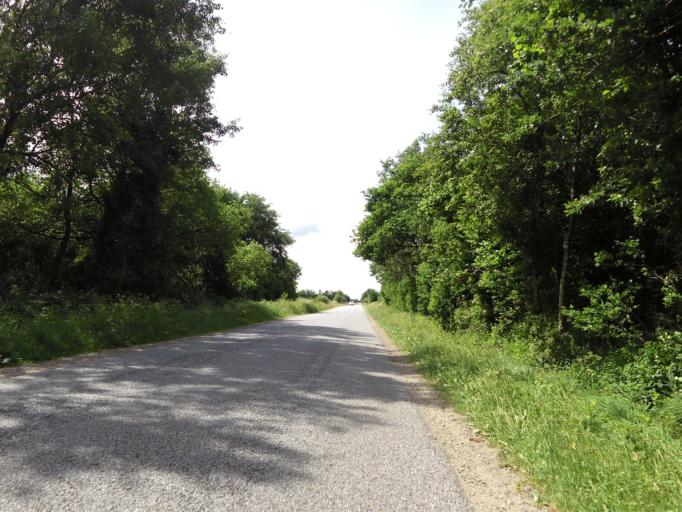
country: DK
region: South Denmark
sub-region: Esbjerg Kommune
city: Ribe
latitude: 55.2613
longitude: 8.8473
